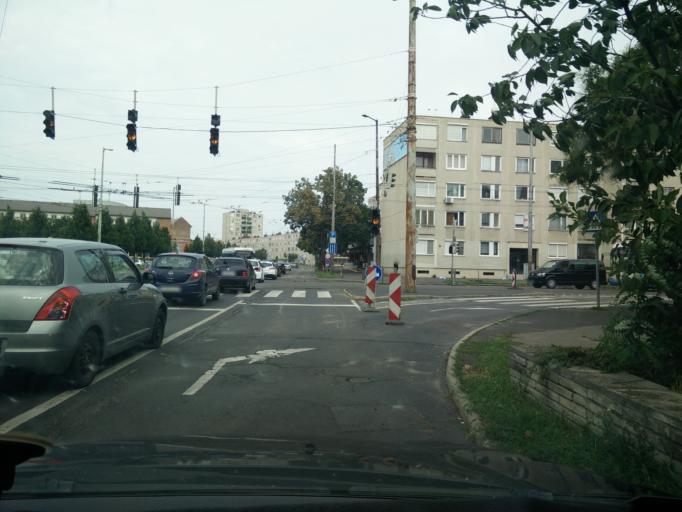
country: HU
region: Hajdu-Bihar
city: Debrecen
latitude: 47.5297
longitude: 21.6316
